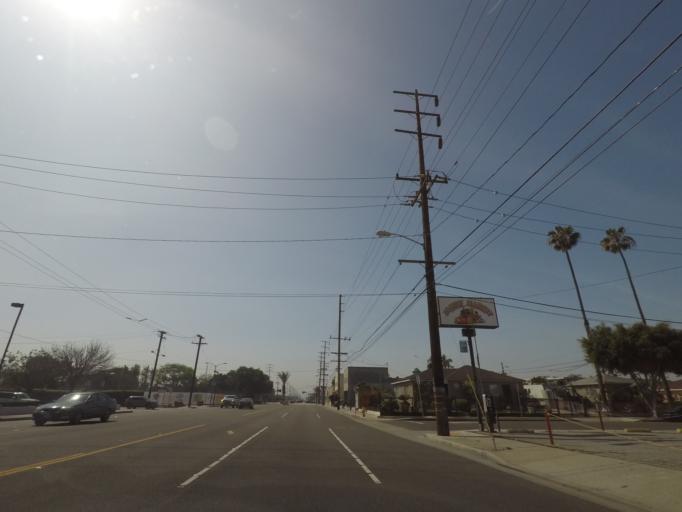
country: US
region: California
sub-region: Los Angeles County
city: Hawthorne
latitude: 33.9184
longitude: -118.3440
